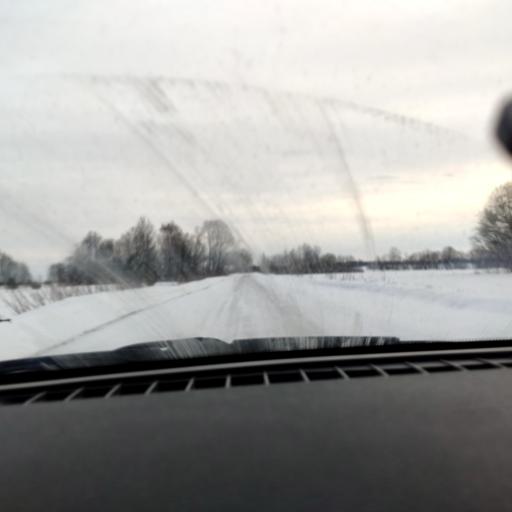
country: RU
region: Bashkortostan
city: Iglino
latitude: 54.7632
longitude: 56.5335
